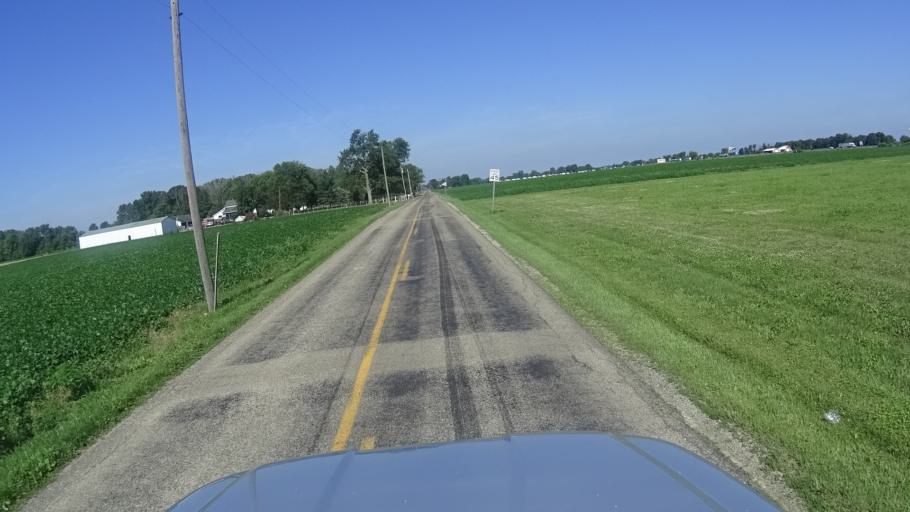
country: US
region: Indiana
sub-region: Madison County
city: Ingalls
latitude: 39.9879
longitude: -85.8153
